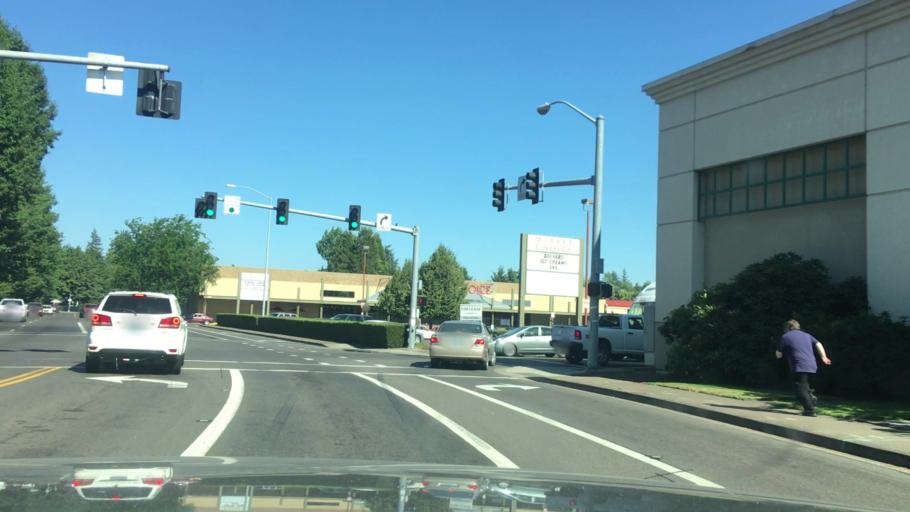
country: US
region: Oregon
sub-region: Lane County
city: Eugene
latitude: 44.0933
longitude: -123.0955
